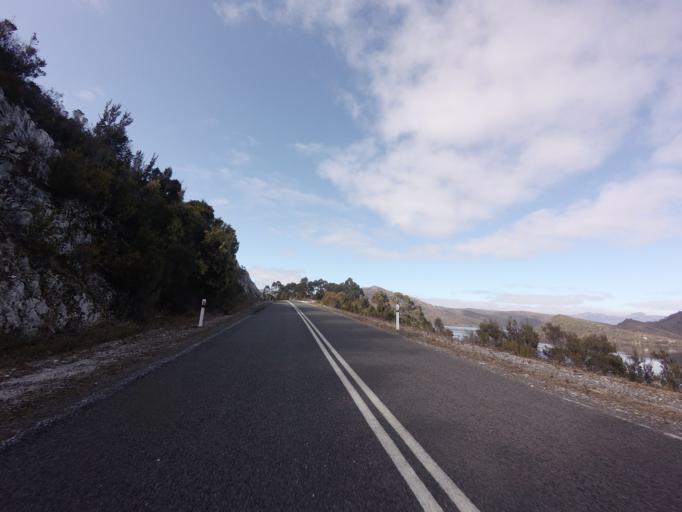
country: AU
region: Tasmania
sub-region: Huon Valley
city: Geeveston
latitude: -42.8323
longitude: 146.1251
